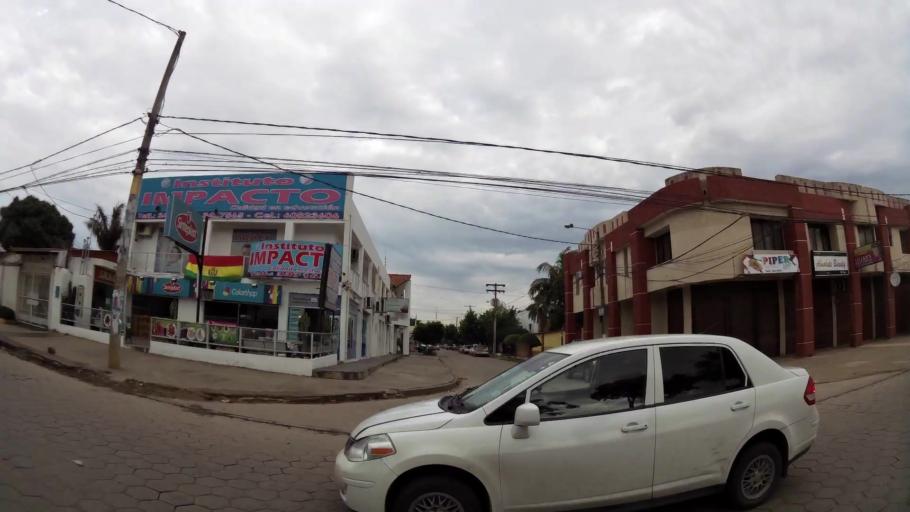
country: BO
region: Santa Cruz
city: Santa Cruz de la Sierra
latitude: -17.7602
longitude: -63.1673
